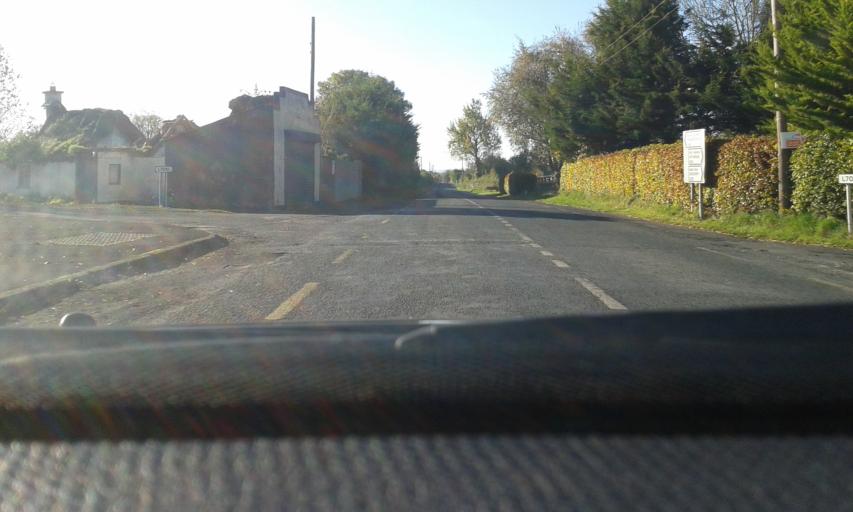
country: IE
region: Leinster
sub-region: Kildare
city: Monasterevin
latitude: 53.1718
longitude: -7.0284
